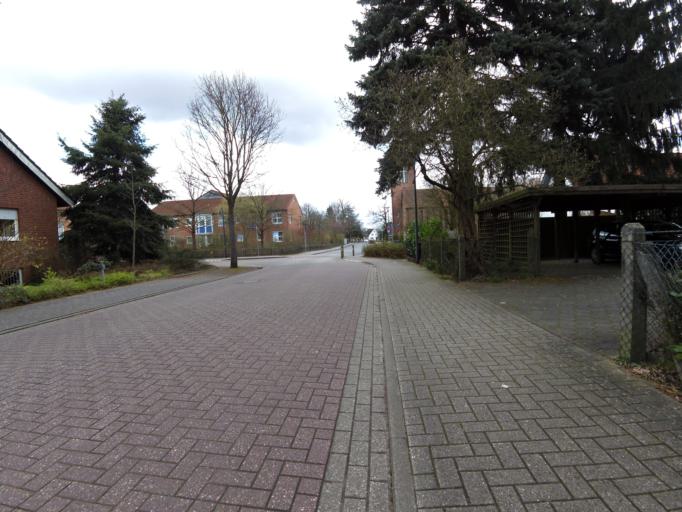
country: DE
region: Lower Saxony
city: Hambuhren
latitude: 52.6029
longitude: 10.0191
